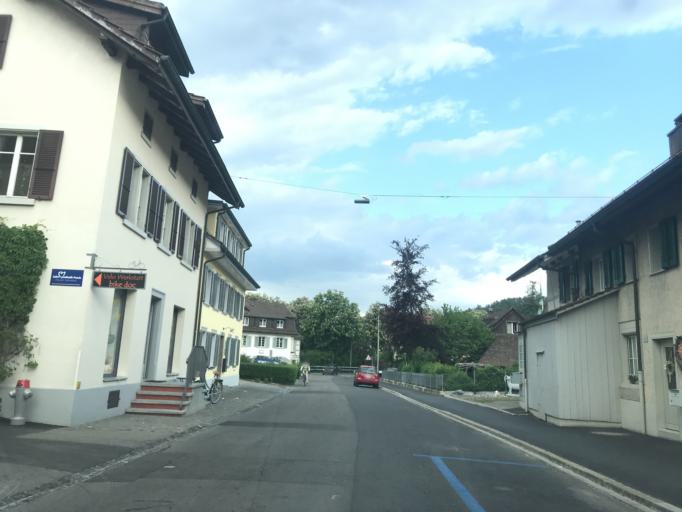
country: CH
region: Zurich
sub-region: Bezirk Winterthur
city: Wuelflingen (Kreis 6) / Lindenplatz
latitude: 47.5089
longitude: 8.6923
